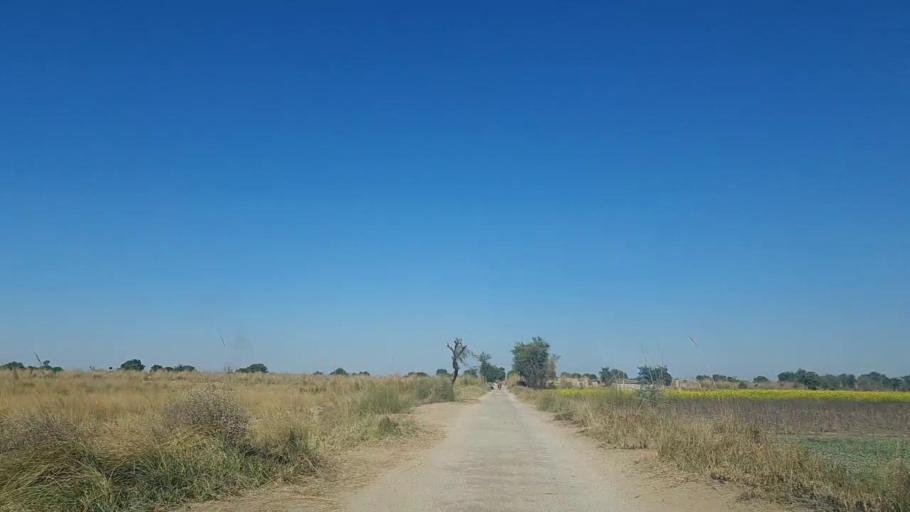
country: PK
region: Sindh
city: Khadro
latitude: 26.2129
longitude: 68.8601
